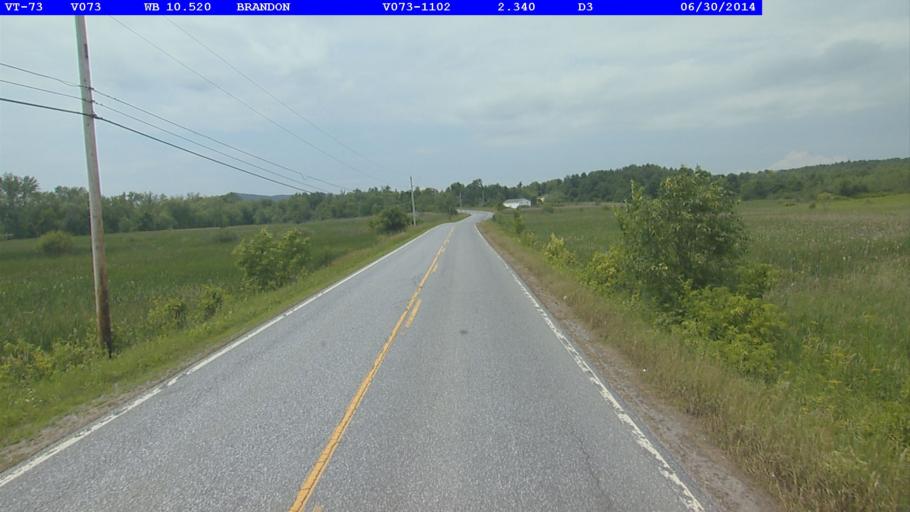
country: US
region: Vermont
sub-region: Rutland County
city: Brandon
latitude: 43.8013
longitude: -73.1072
